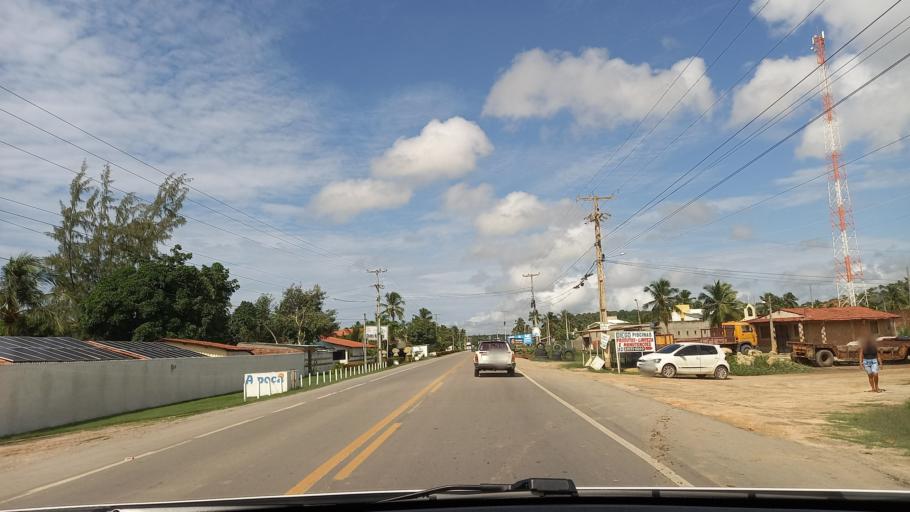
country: BR
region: Pernambuco
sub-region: Sao Jose Da Coroa Grande
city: Sao Jose da Coroa Grande
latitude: -8.9362
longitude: -35.1695
